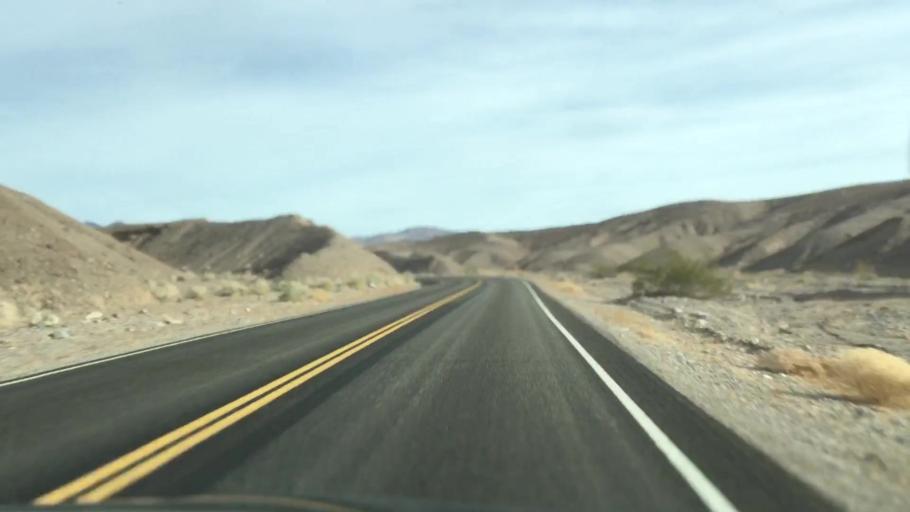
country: US
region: Nevada
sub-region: Nye County
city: Beatty
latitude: 36.6685
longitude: -117.0152
